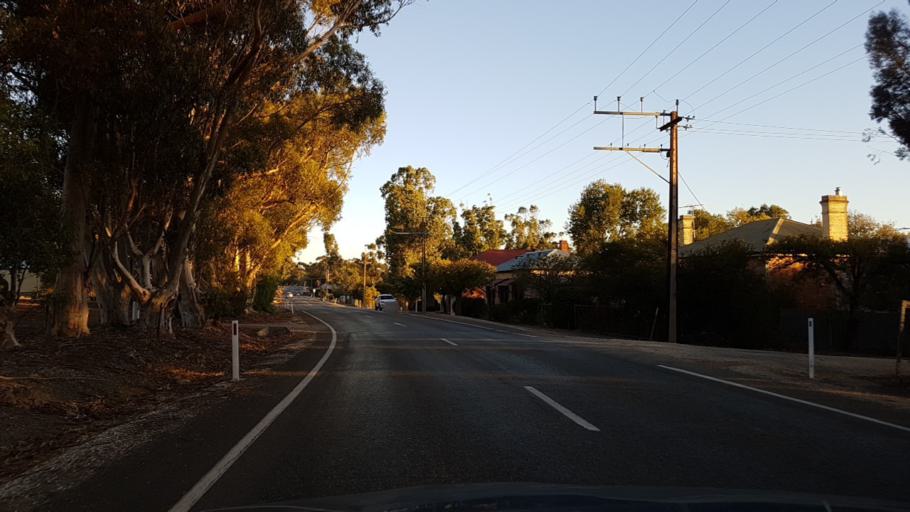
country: AU
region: South Australia
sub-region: Wakefield
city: Balaklava
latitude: -34.1450
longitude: 138.6889
